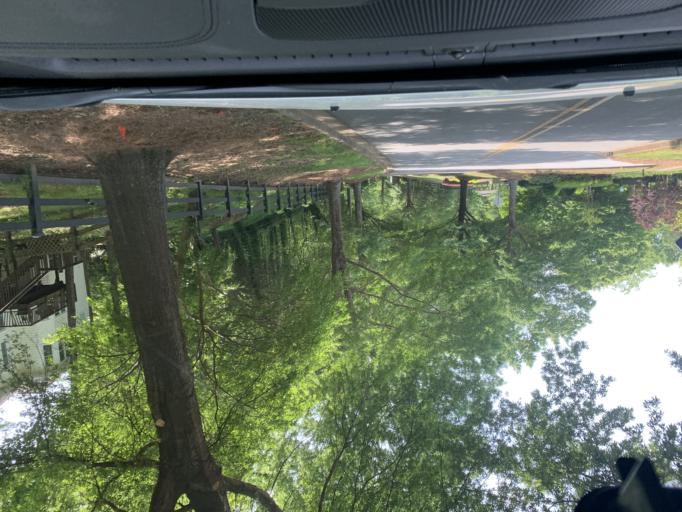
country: US
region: Georgia
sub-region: Fulton County
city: Johns Creek
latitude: 34.1208
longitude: -84.1979
